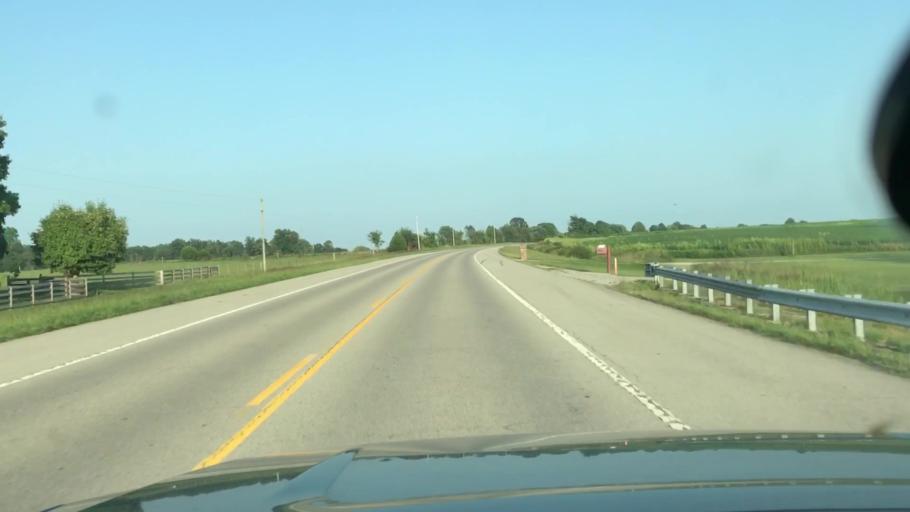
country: US
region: Tennessee
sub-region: Sumner County
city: Portland
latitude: 36.5769
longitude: -86.3968
